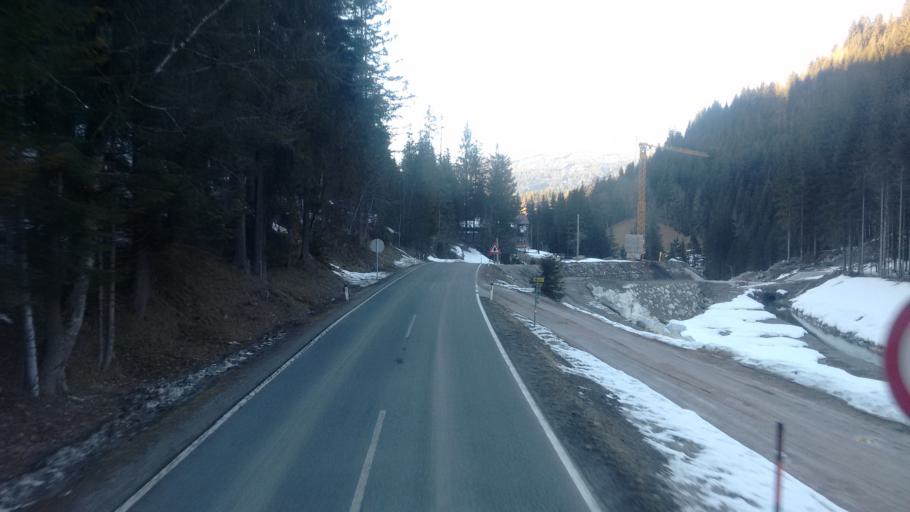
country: AT
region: Salzburg
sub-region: Politischer Bezirk Sankt Johann im Pongau
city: Altenmarkt im Pongau
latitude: 47.3498
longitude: 13.4288
